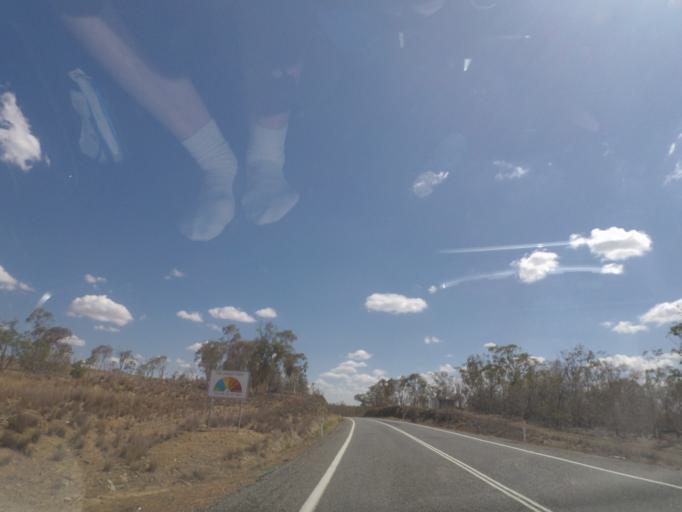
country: AU
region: Queensland
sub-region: Southern Downs
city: Warwick
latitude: -28.2092
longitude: 151.5655
